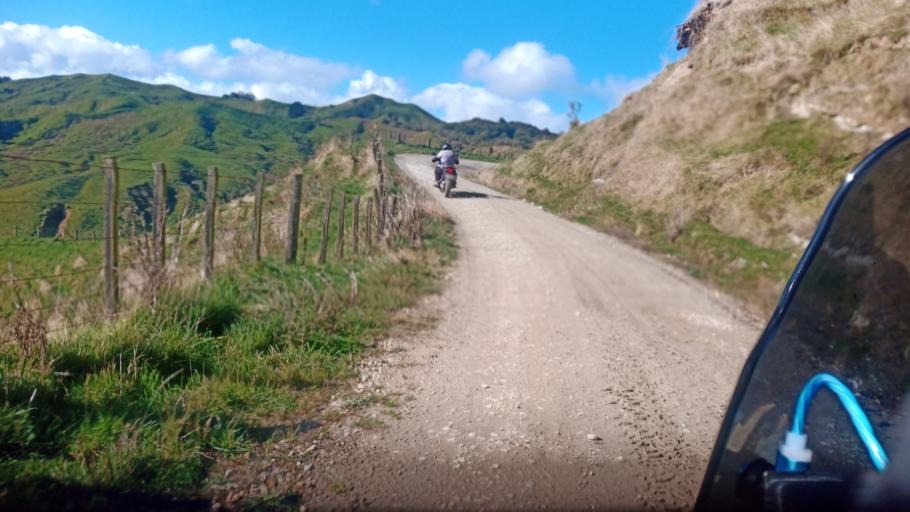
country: NZ
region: Hawke's Bay
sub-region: Wairoa District
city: Wairoa
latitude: -38.6656
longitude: 177.5222
